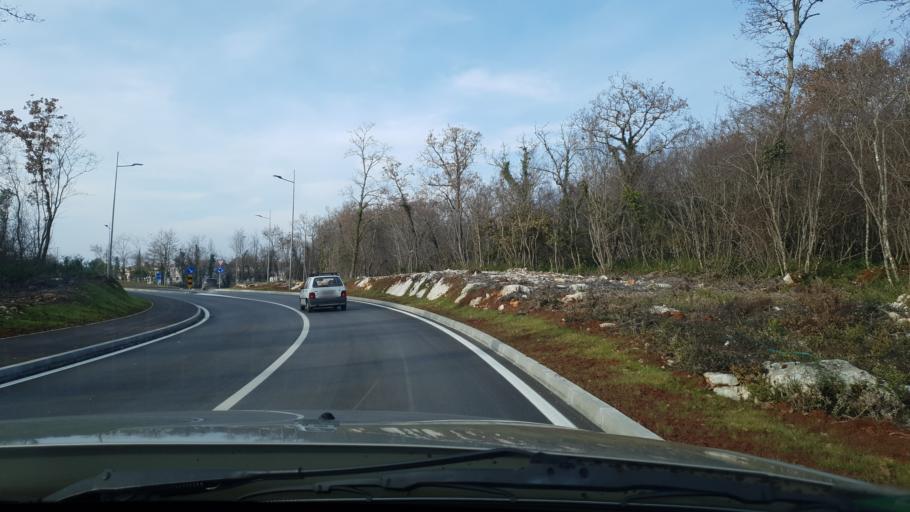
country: HR
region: Istarska
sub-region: Grad Porec
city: Porec
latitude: 45.2351
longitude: 13.6122
